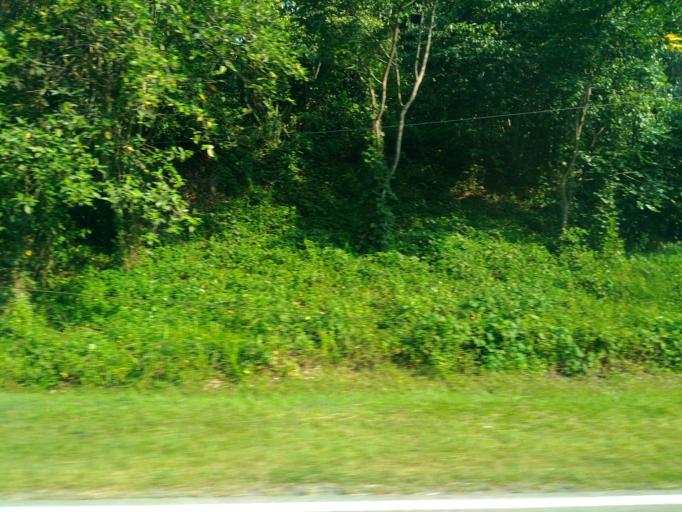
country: MY
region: Sabah
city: Taman Rajawali
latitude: 5.6978
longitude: 117.4023
